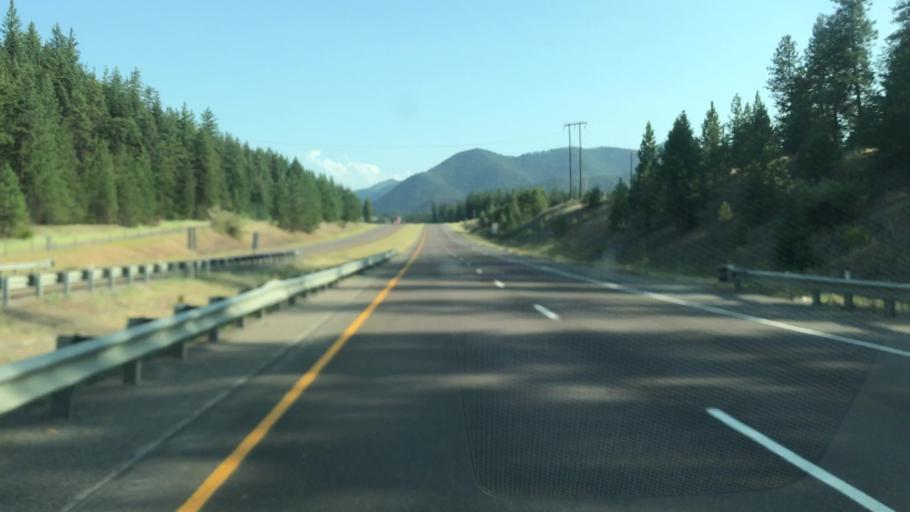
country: US
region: Montana
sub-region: Mineral County
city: Superior
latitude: 47.0670
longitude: -114.7644
